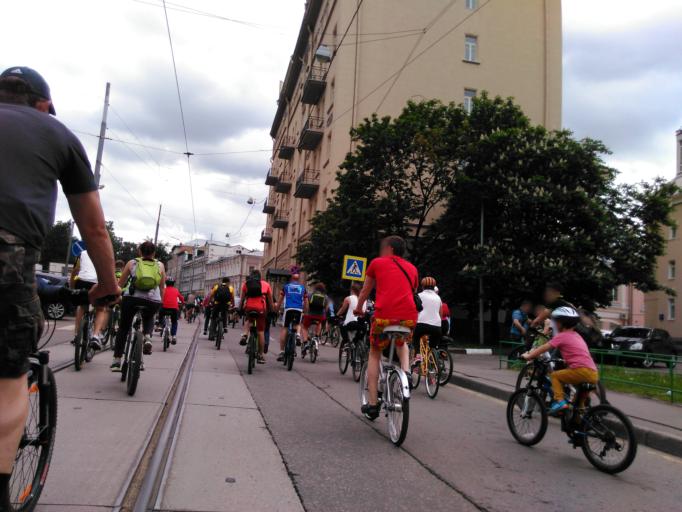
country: RU
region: Moscow
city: Zamoskvorech'ye
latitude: 55.7587
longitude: 37.6457
